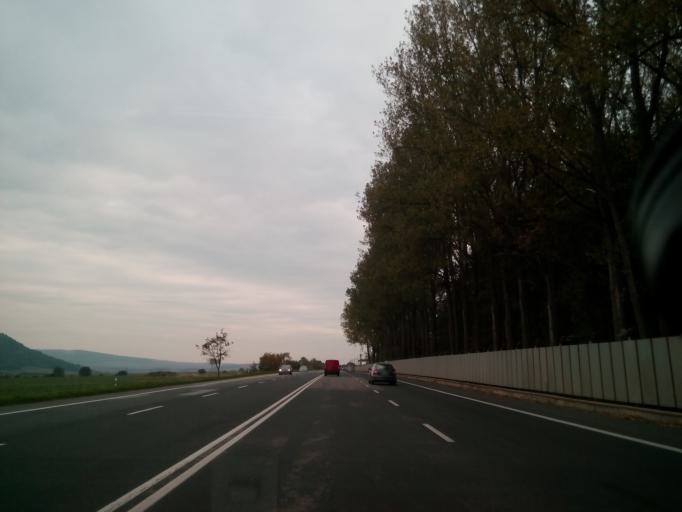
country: SK
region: Presovsky
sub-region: Okres Presov
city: Presov
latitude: 49.0293
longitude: 21.2970
